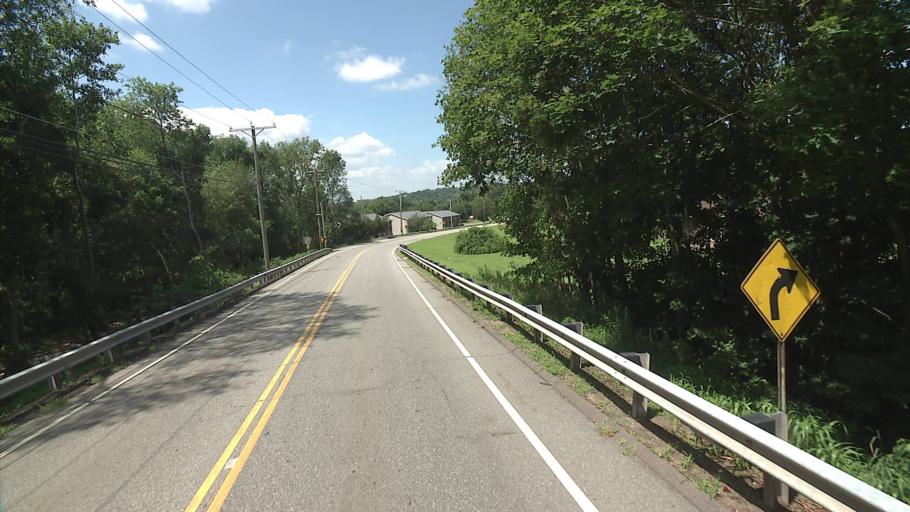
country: US
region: Connecticut
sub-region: Windham County
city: Willimantic
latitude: 41.7137
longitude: -72.1862
